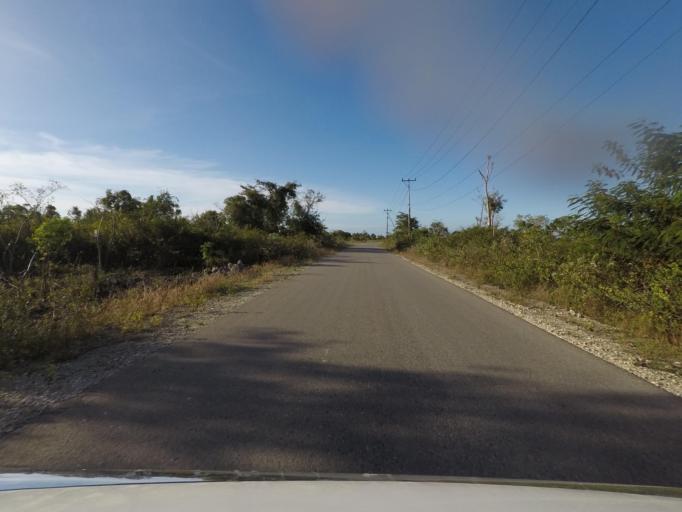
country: TL
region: Lautem
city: Lospalos
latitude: -8.3761
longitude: 127.0153
